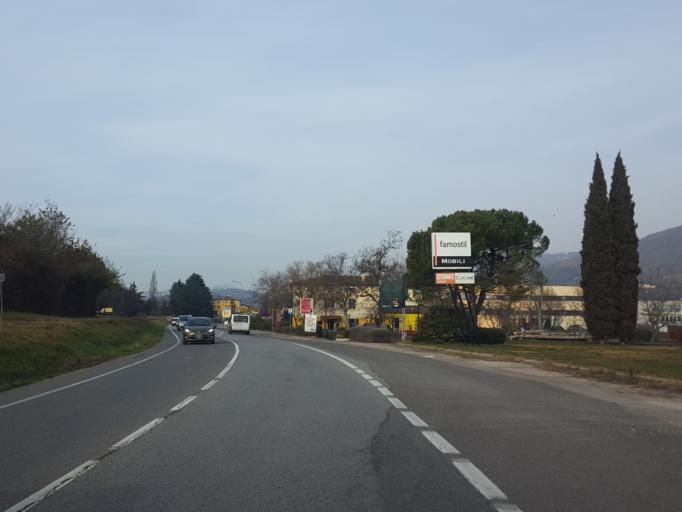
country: IT
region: Veneto
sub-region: Provincia di Verona
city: Costermano
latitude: 45.5839
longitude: 10.7515
